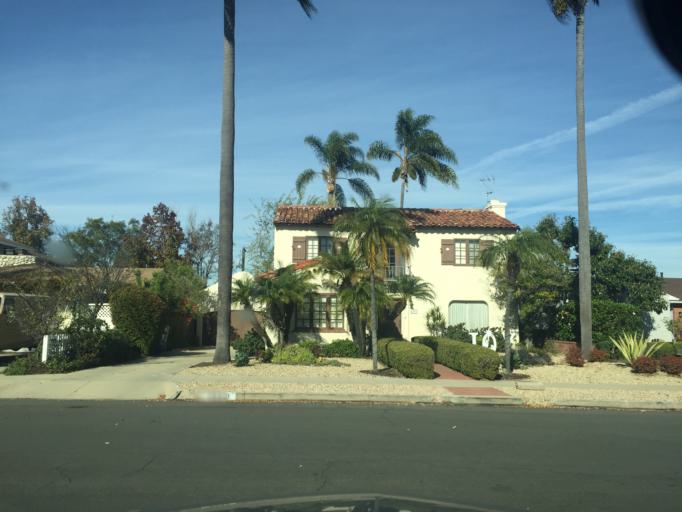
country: US
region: California
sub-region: San Diego County
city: Lemon Grove
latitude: 32.7717
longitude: -117.1023
